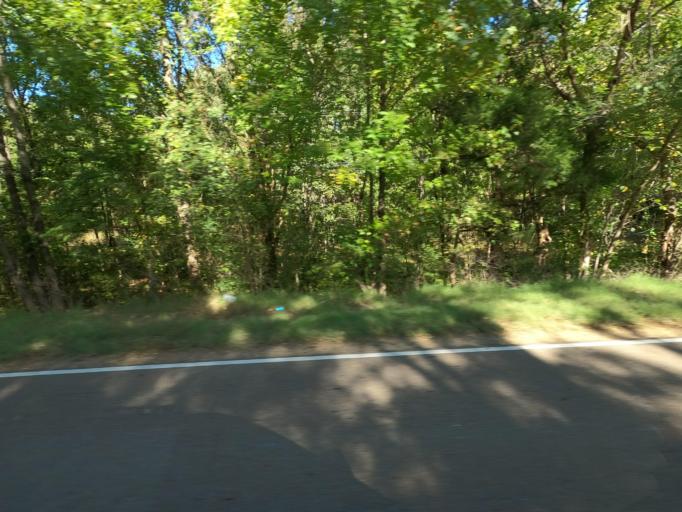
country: US
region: Tennessee
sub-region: Shelby County
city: Arlington
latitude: 35.2551
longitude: -89.6569
